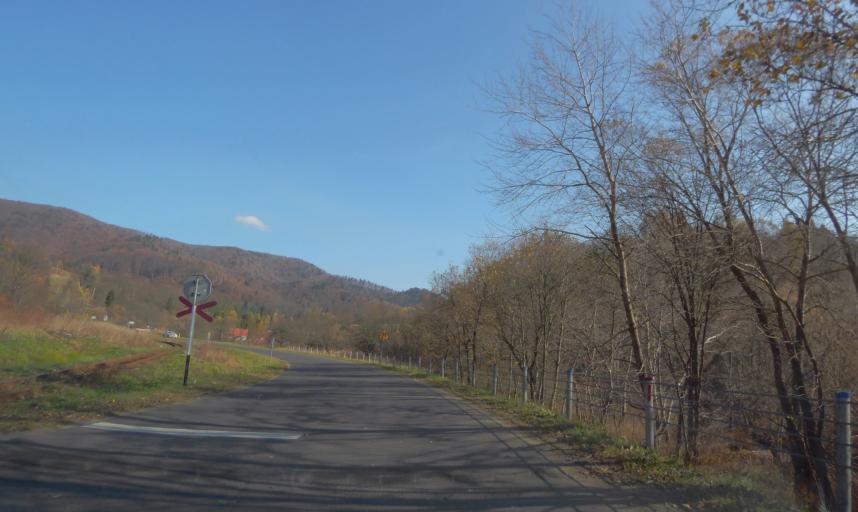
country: PL
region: Subcarpathian Voivodeship
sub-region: Powiat leski
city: Cisna
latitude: 49.2065
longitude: 22.2620
